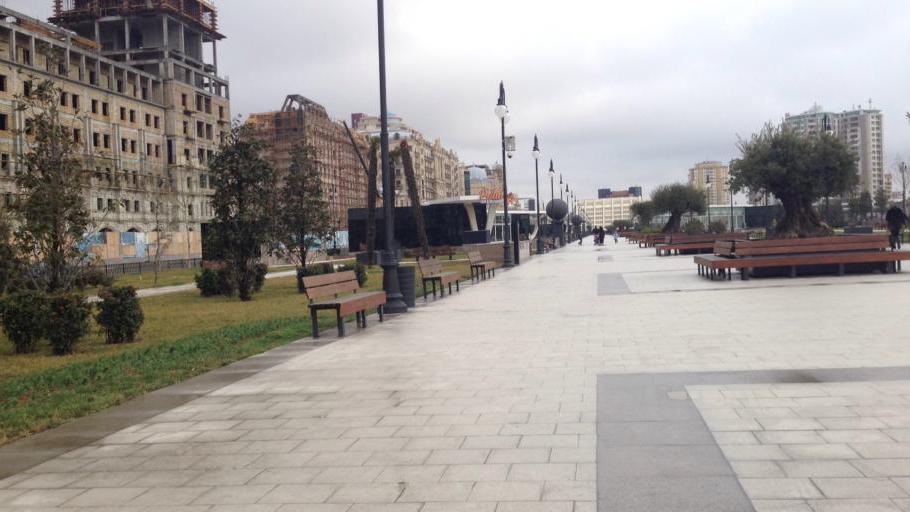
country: AZ
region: Baki
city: Badamdar
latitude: 40.3749
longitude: 49.8353
